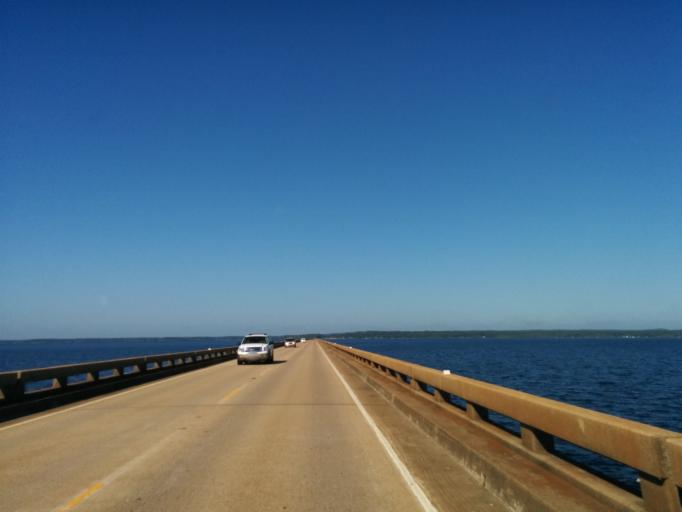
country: US
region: Texas
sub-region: Sabine County
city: Milam
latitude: 31.4850
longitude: -93.7151
